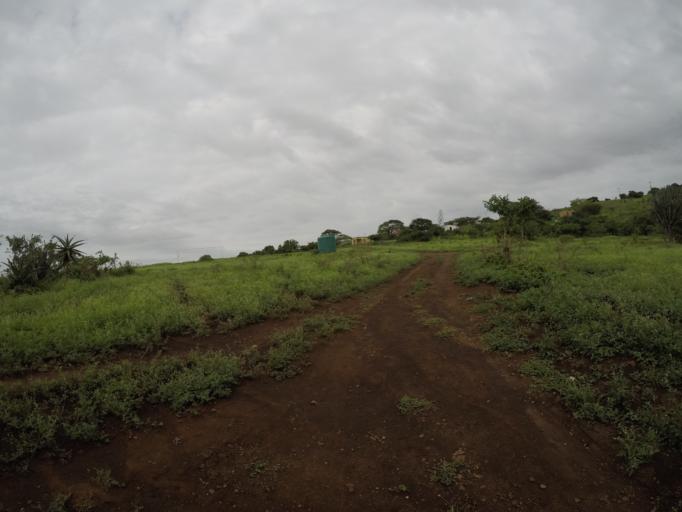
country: ZA
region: KwaZulu-Natal
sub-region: uThungulu District Municipality
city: Empangeni
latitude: -28.6401
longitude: 31.9086
